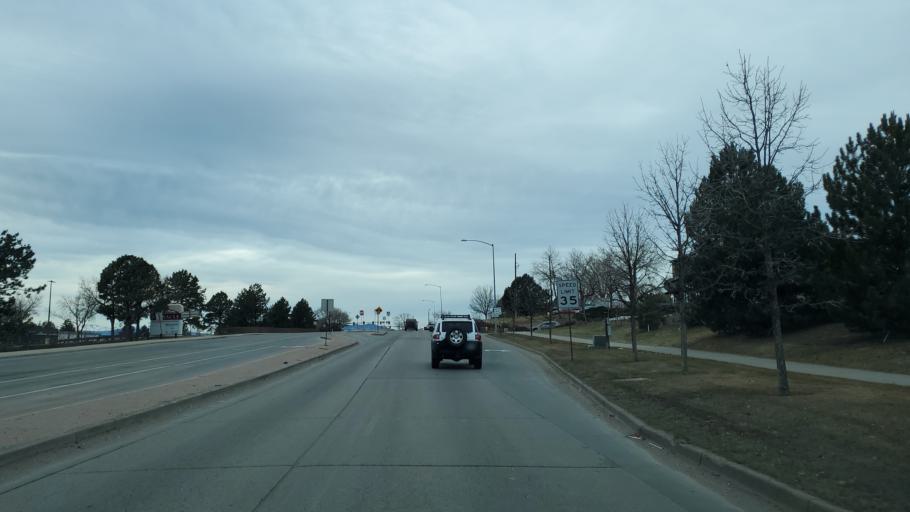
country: US
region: Colorado
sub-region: Adams County
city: Thornton
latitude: 39.8708
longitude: -104.9782
